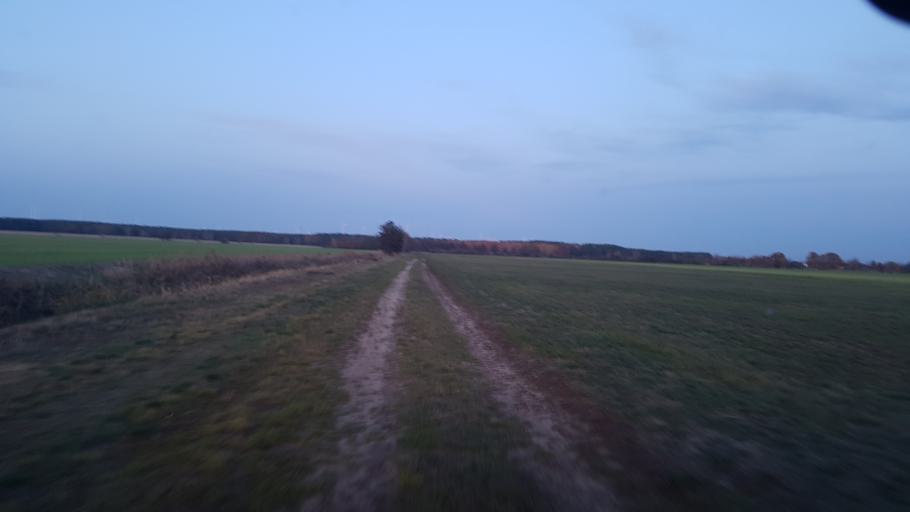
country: DE
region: Brandenburg
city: Schilda
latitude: 51.6294
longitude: 13.3338
